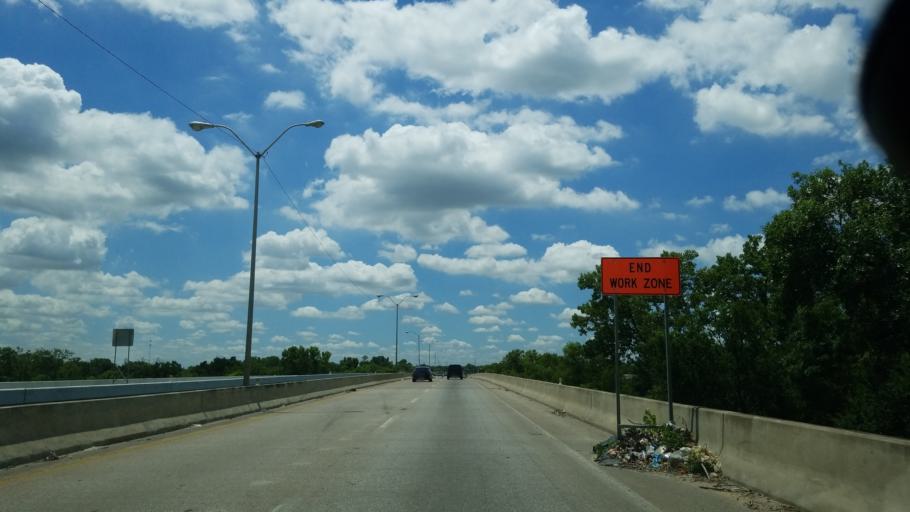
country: US
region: Texas
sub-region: Dallas County
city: Dallas
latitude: 32.7290
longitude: -96.7581
